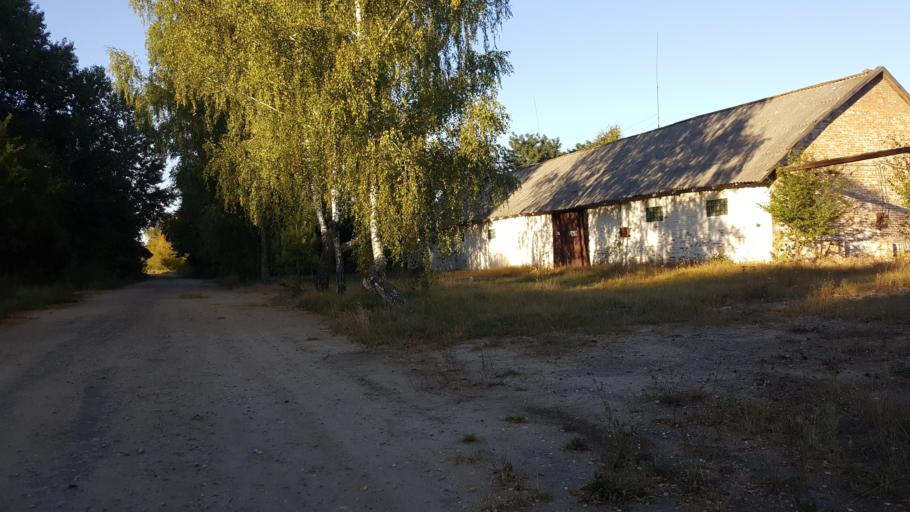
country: BY
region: Brest
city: Vysokaye
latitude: 52.3197
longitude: 23.4318
